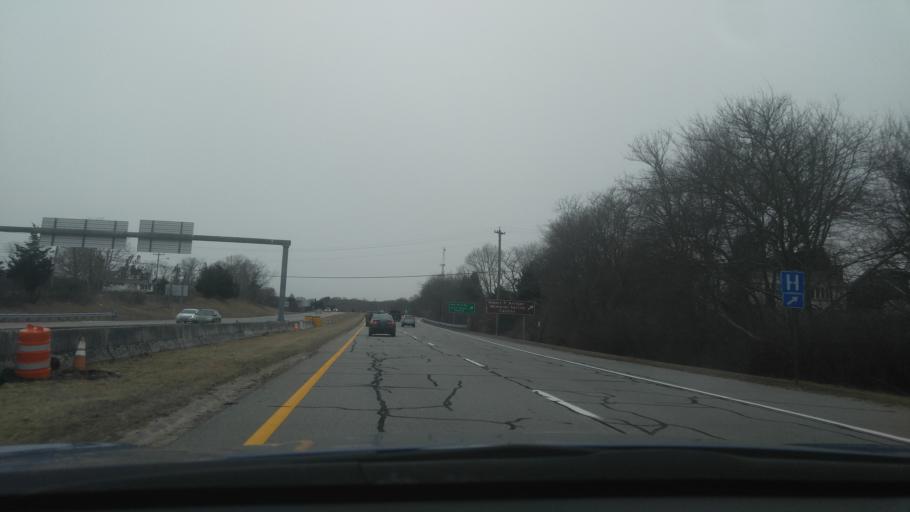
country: US
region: Rhode Island
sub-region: Washington County
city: Wakefield-Peacedale
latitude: 41.4303
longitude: -71.4889
